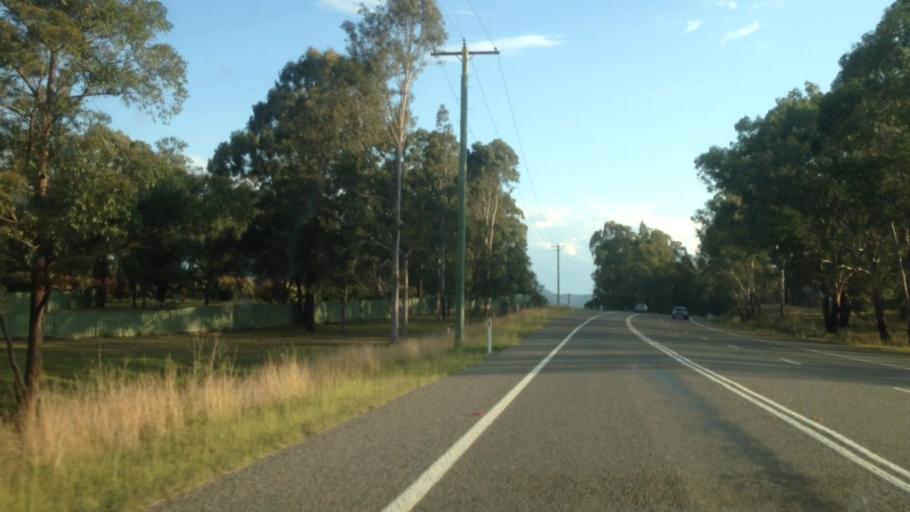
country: AU
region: New South Wales
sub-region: Cessnock
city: Kurri Kurri
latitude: -32.8590
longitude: 151.4843
